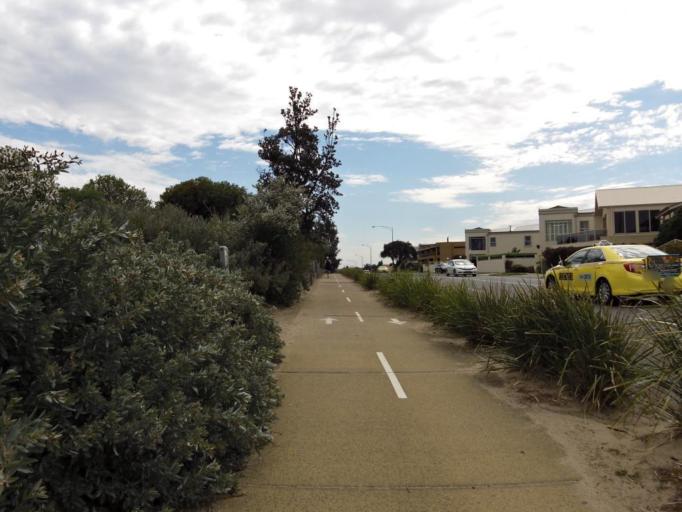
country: AU
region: Victoria
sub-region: Bayside
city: Black Rock
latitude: -37.9637
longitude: 145.0120
